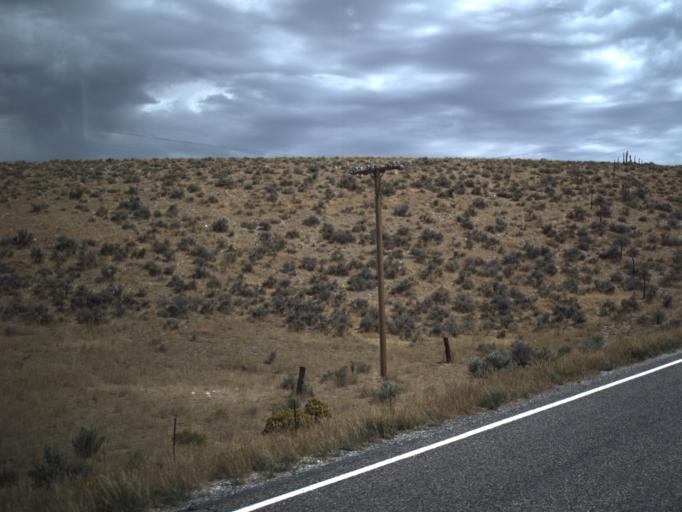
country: US
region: Idaho
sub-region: Cassia County
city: Burley
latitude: 41.8155
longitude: -113.2253
